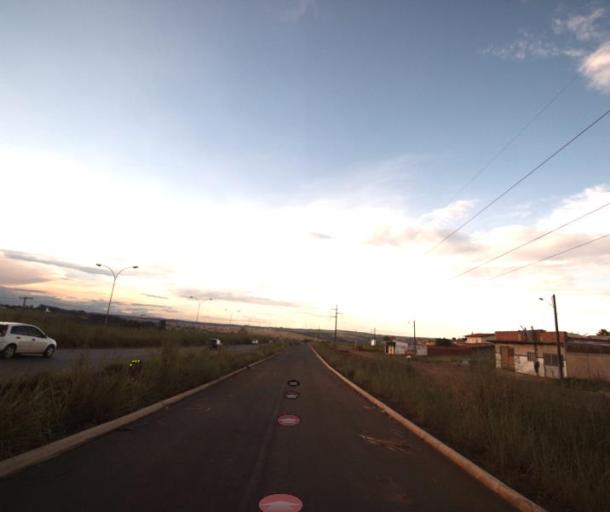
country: BR
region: Goias
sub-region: Anapolis
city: Anapolis
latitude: -16.3215
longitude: -48.9217
